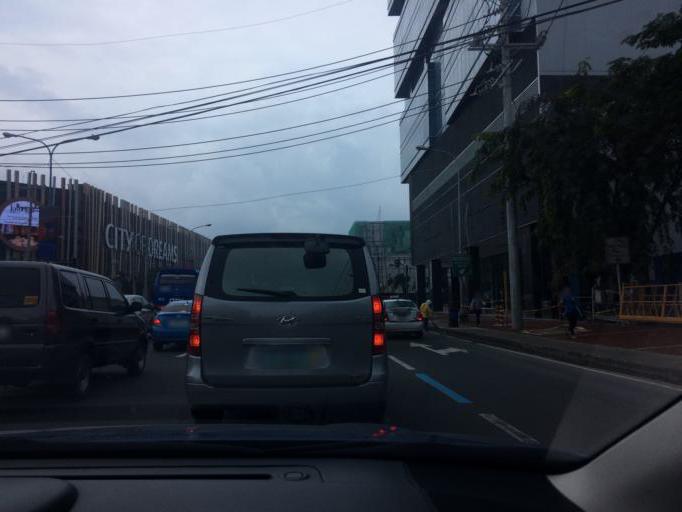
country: PH
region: Metro Manila
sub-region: Makati City
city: Makati City
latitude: 14.5260
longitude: 120.9901
